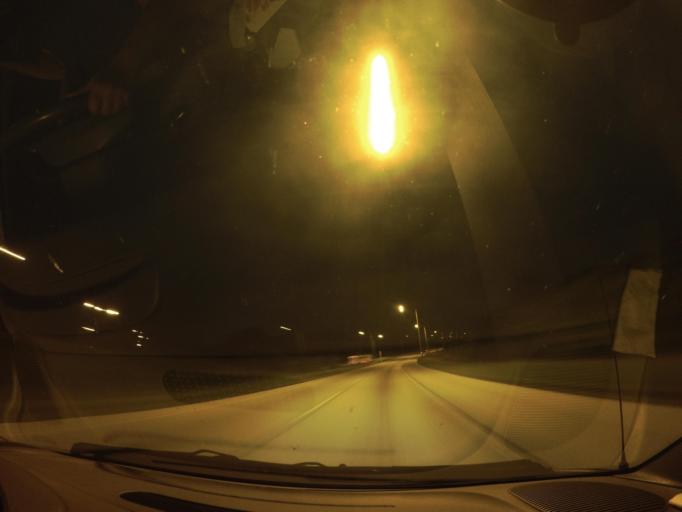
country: US
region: Illinois
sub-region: Cook County
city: Country Club Hills
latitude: 41.5666
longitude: -87.7452
